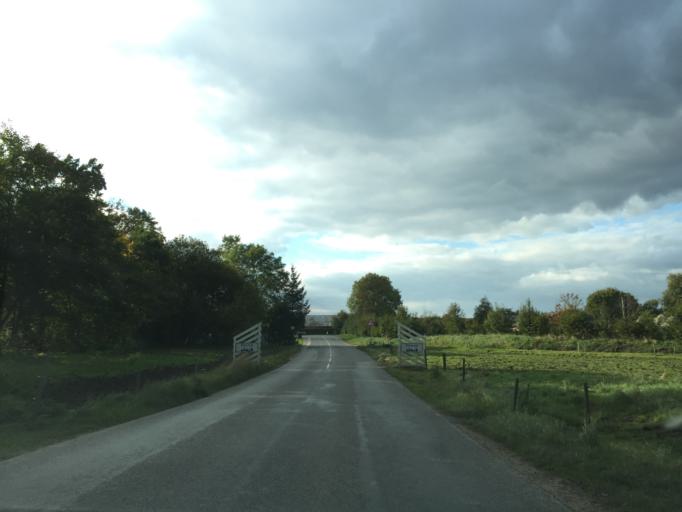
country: DK
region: Central Jutland
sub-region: Favrskov Kommune
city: Ulstrup
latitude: 56.2814
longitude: 9.7467
